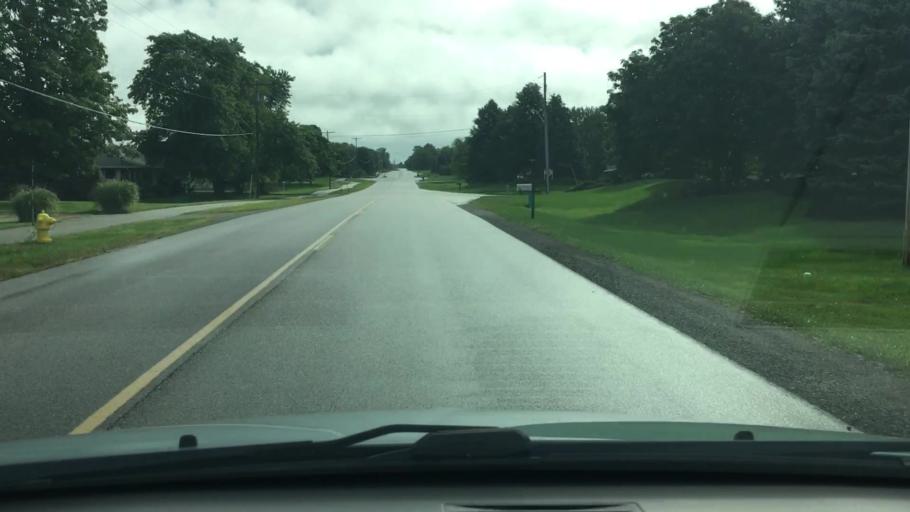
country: US
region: Michigan
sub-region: Ottawa County
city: Hudsonville
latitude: 42.8403
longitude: -85.8581
